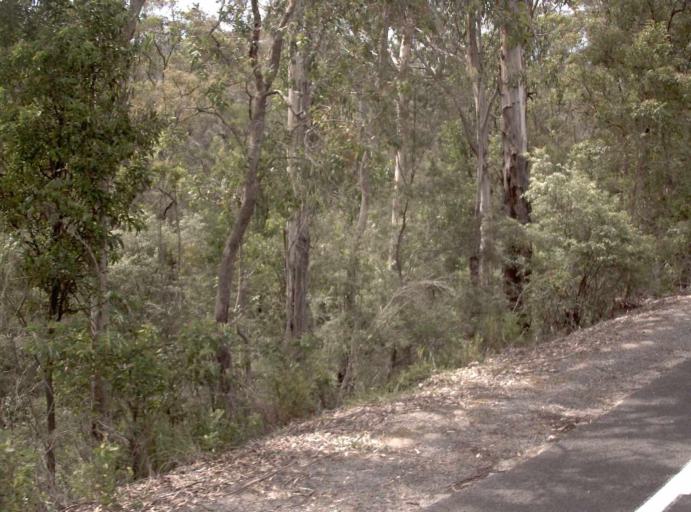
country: AU
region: New South Wales
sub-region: Bega Valley
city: Eden
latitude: -37.4597
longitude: 149.5908
